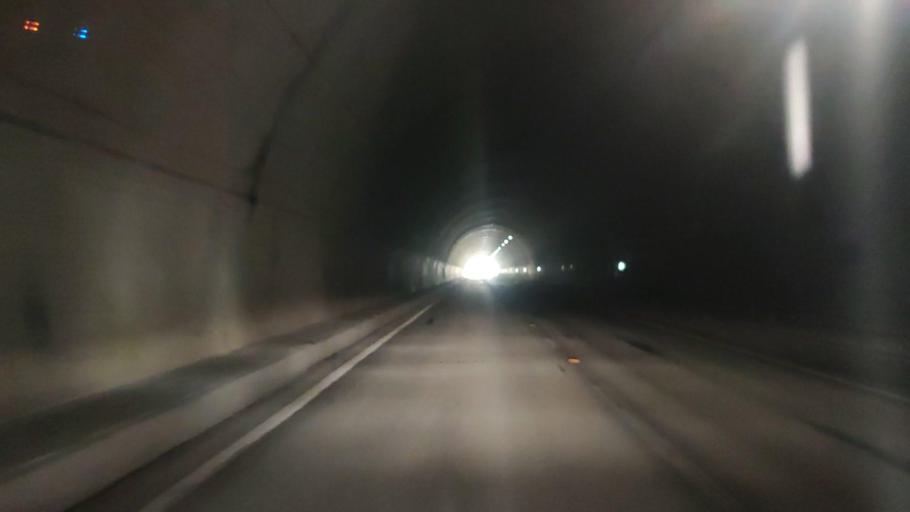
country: JP
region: Miyazaki
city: Nobeoka
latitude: 32.7373
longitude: 131.8248
